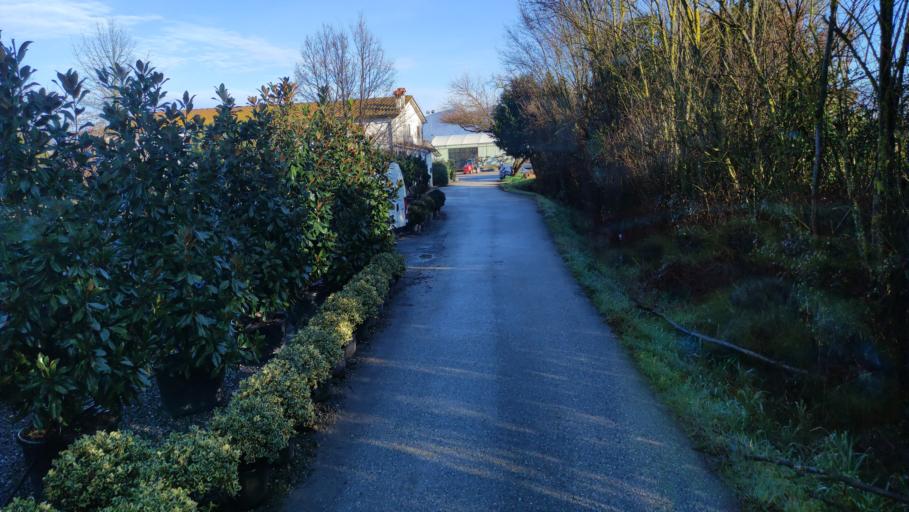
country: IT
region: Tuscany
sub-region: Provincia di Pistoia
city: Cantagrillo-Casalguidi
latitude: 43.8728
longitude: 10.9369
